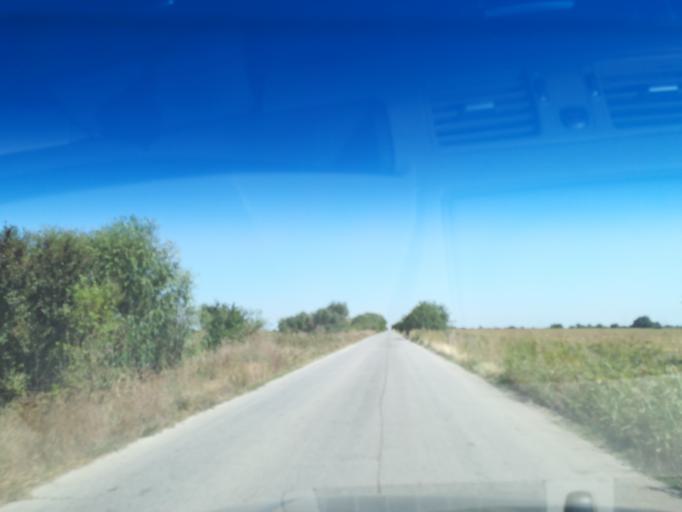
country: BG
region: Plovdiv
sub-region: Obshtina Suedinenie
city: Suedinenie
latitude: 42.2514
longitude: 24.4693
